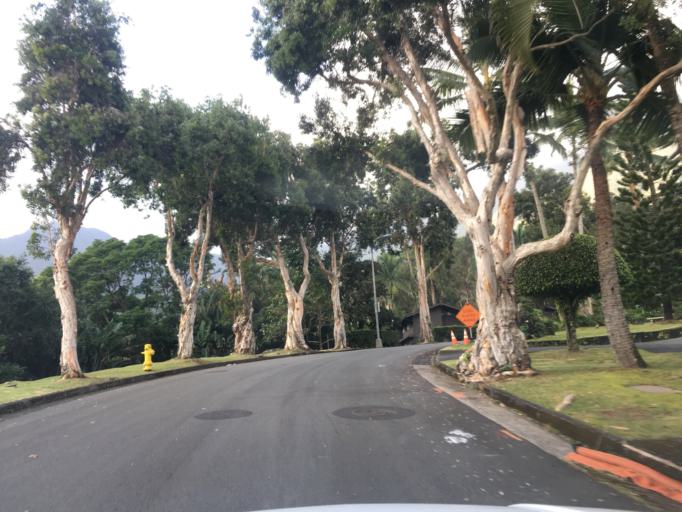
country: US
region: Hawaii
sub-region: Honolulu County
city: Maunawili
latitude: 21.3580
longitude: -157.7698
